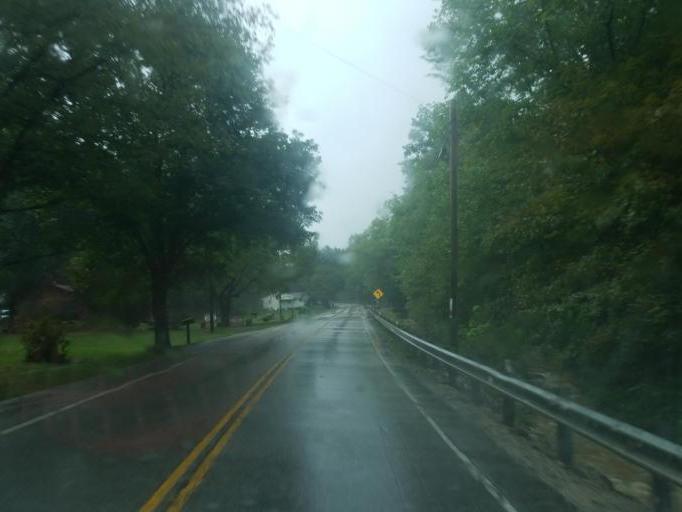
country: US
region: Kentucky
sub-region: Rowan County
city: Morehead
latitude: 38.2665
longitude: -83.3308
